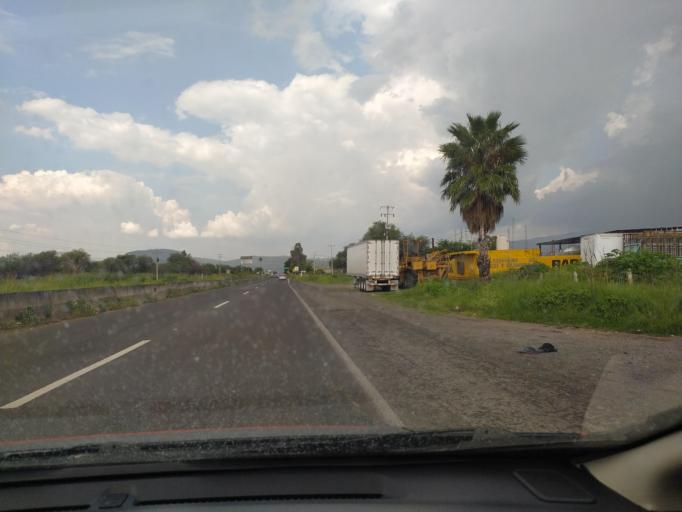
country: MX
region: Jalisco
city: Bellavista
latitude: 20.4147
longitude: -103.6316
